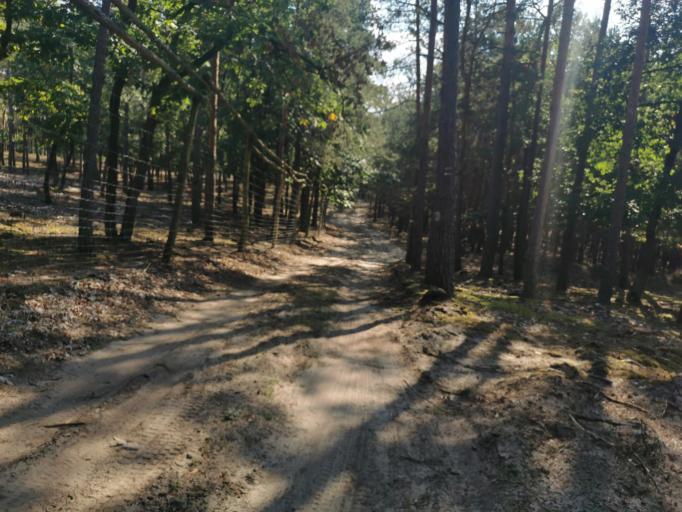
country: SK
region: Trnavsky
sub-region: Okres Senica
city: Senica
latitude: 48.6170
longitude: 17.2784
